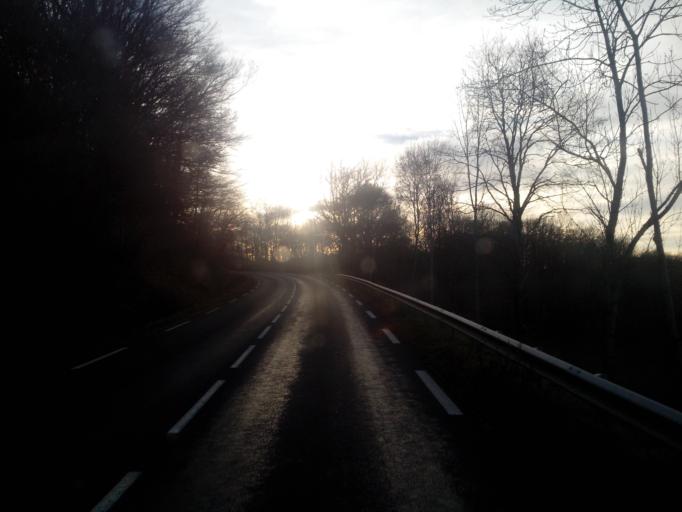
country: FR
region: Auvergne
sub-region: Departement du Cantal
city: Riom-es-Montagnes
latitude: 45.3083
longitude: 2.6066
